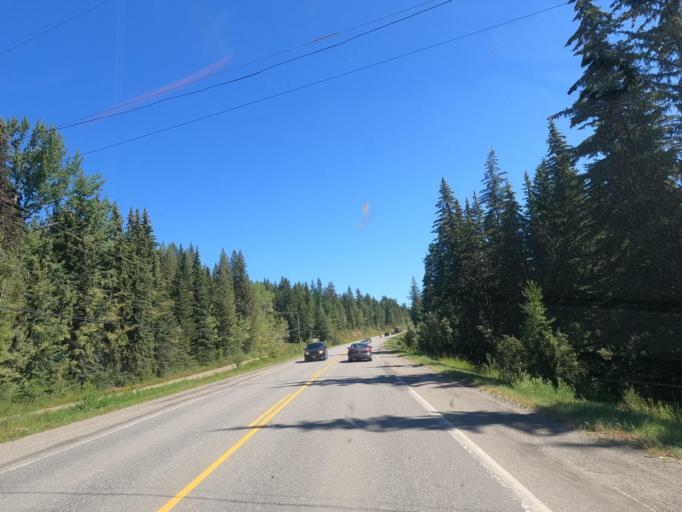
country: CA
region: British Columbia
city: Quesnel
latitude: 53.0462
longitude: -122.4665
